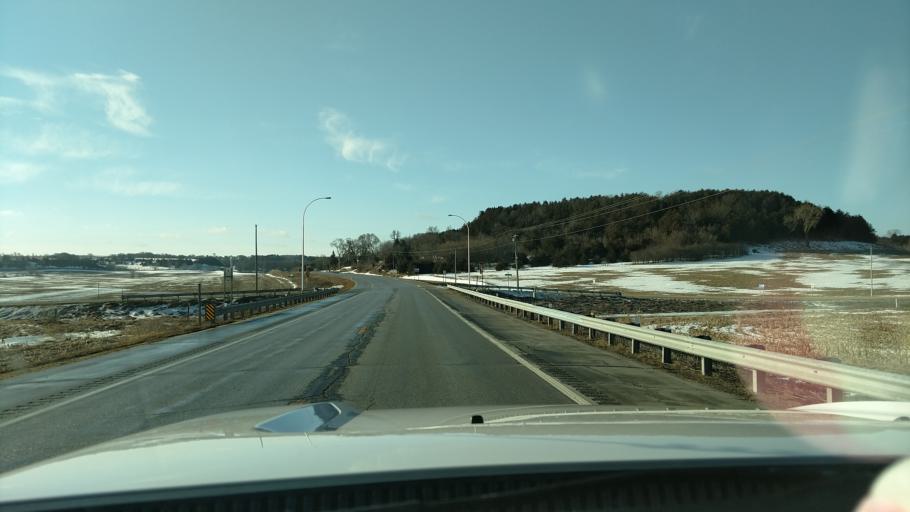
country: US
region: Minnesota
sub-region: Olmsted County
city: Oronoco
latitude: 44.1379
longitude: -92.4167
